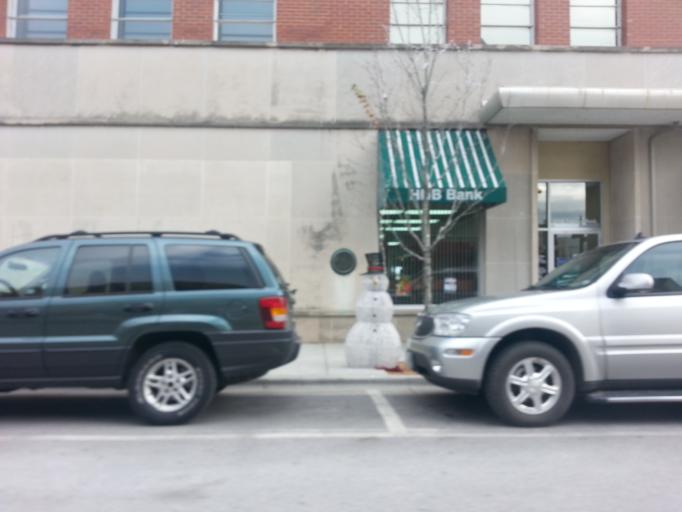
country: US
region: Missouri
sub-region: Marion County
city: Hannibal
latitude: 39.7099
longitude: -91.3558
